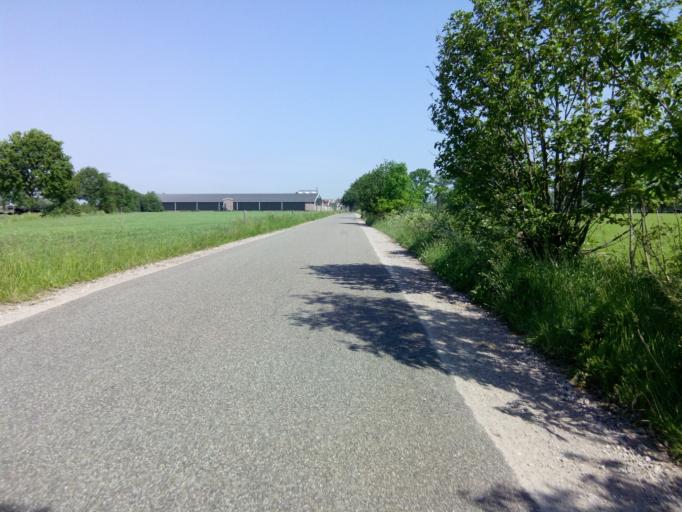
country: NL
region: Utrecht
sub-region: Gemeente Woudenberg
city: Woudenberg
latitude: 52.0664
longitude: 5.4493
